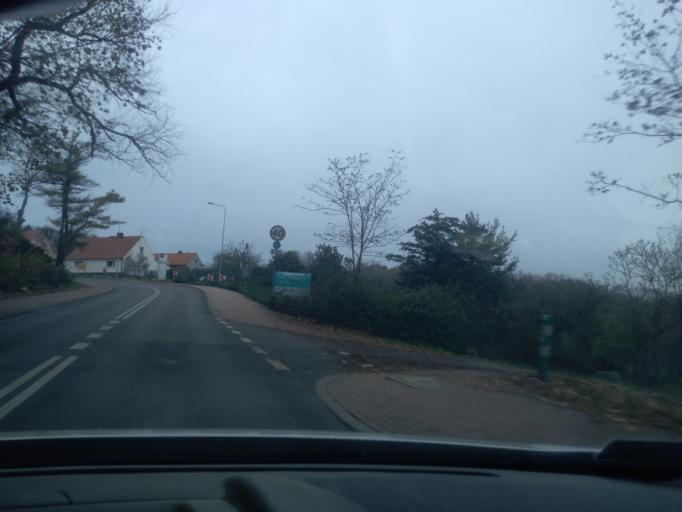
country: PL
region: Greater Poland Voivodeship
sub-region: Powiat poznanski
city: Murowana Goslina
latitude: 52.5435
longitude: 16.9517
